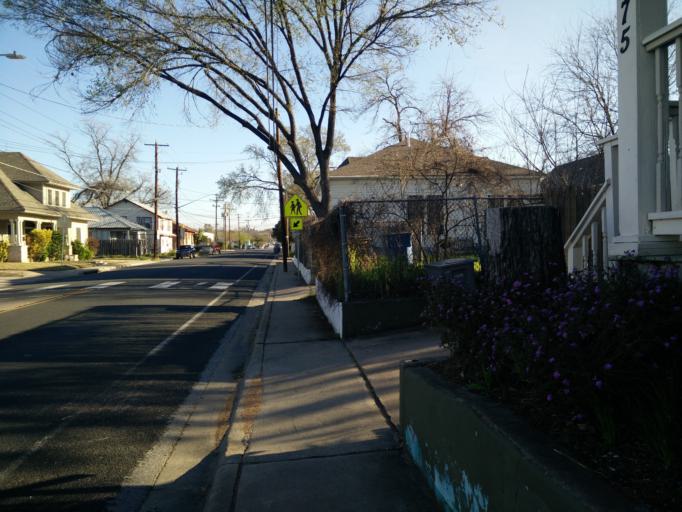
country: US
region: Texas
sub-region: Travis County
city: Austin
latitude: 30.2579
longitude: -97.7335
